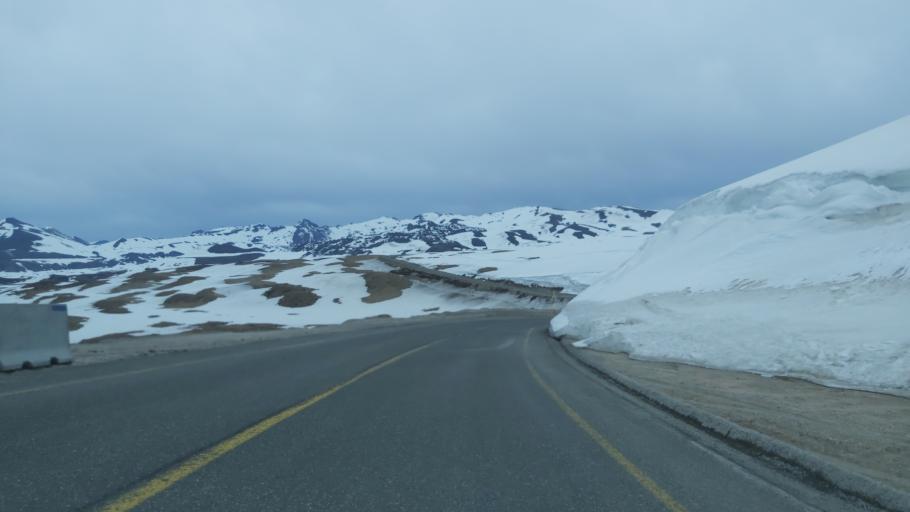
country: CL
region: Maule
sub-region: Provincia de Linares
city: Colbun
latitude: -36.0195
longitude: -70.5227
